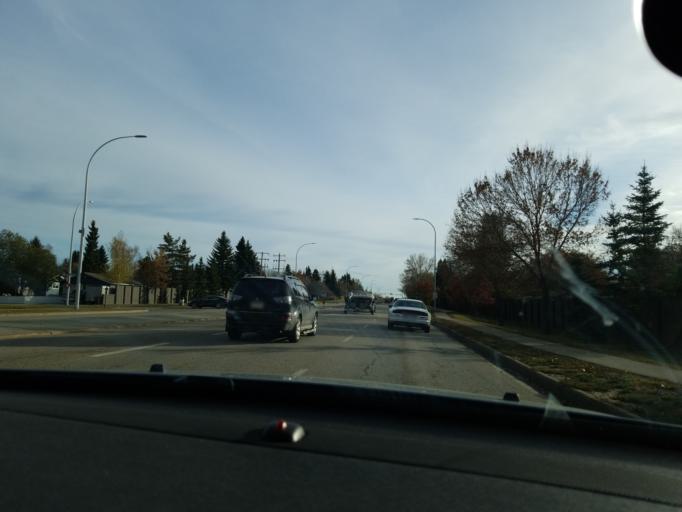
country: CA
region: Alberta
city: Sherwood Park
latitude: 53.5389
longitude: -113.2957
